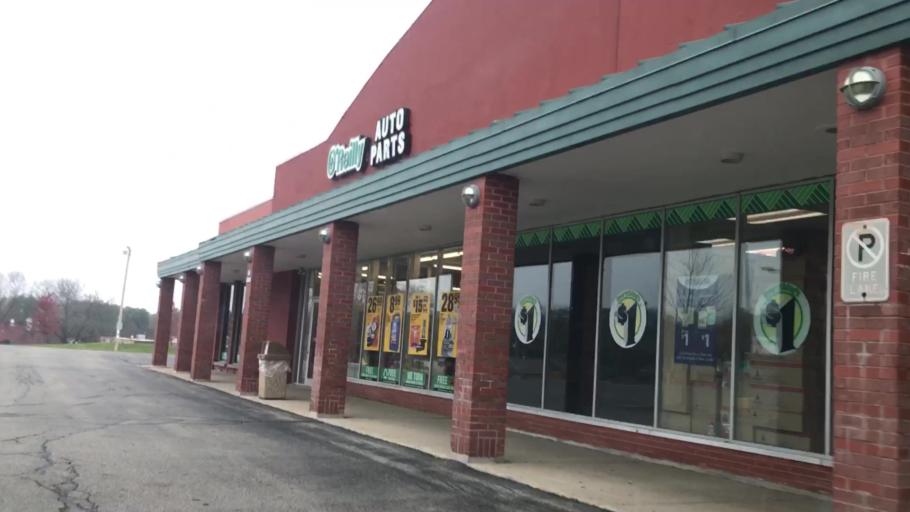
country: US
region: Wisconsin
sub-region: Waukesha County
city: Menomonee Falls
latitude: 43.1709
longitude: -88.1051
